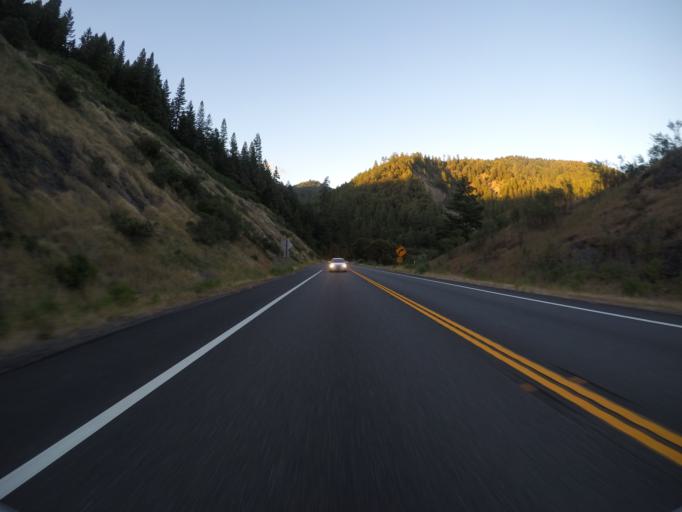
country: US
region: California
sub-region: Humboldt County
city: Redway
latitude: 39.9066
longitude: -123.7565
